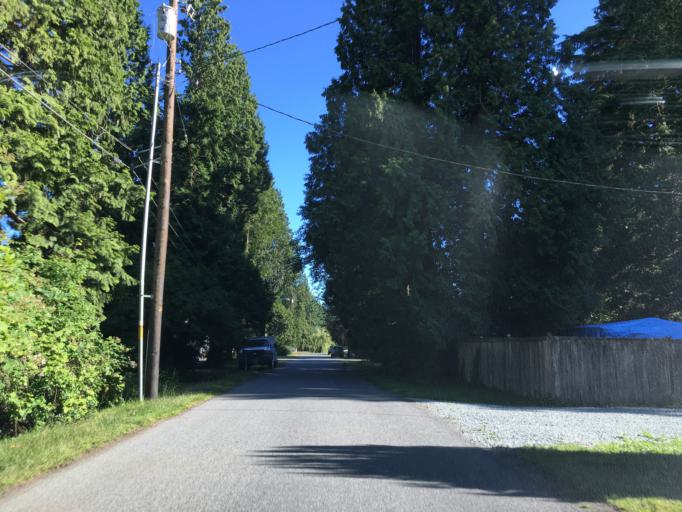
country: US
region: Washington
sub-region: Whatcom County
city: Birch Bay
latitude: 48.9424
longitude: -122.7556
